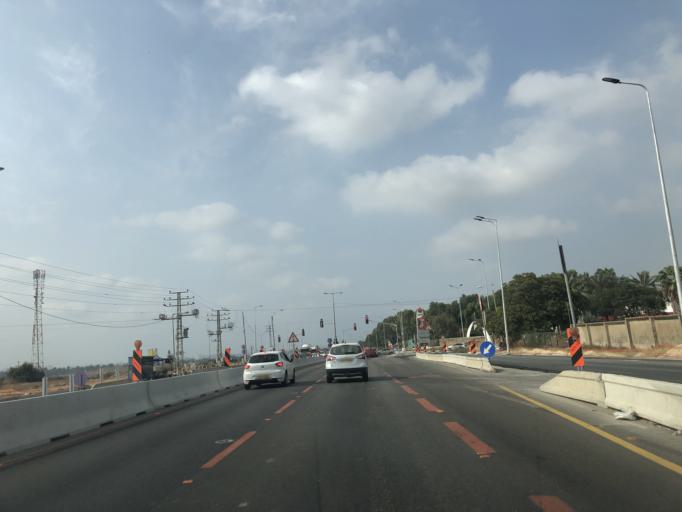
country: IL
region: Central District
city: Rosh Ha'Ayin
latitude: 32.0922
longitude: 34.9414
